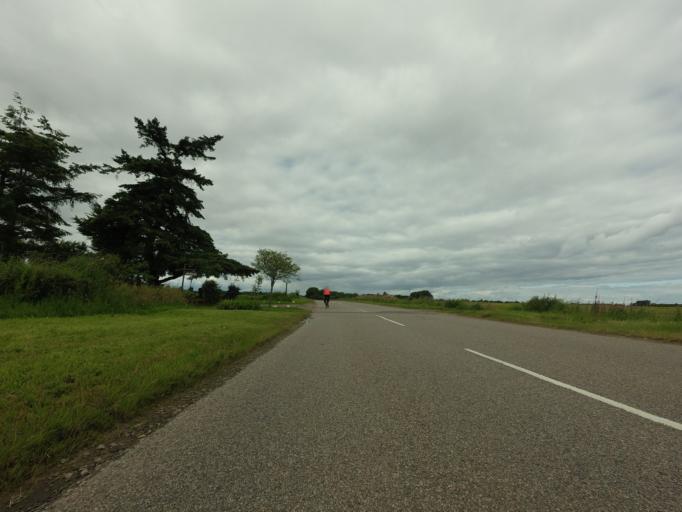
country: GB
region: Scotland
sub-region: Moray
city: Kinloss
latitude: 57.6294
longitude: -3.5512
